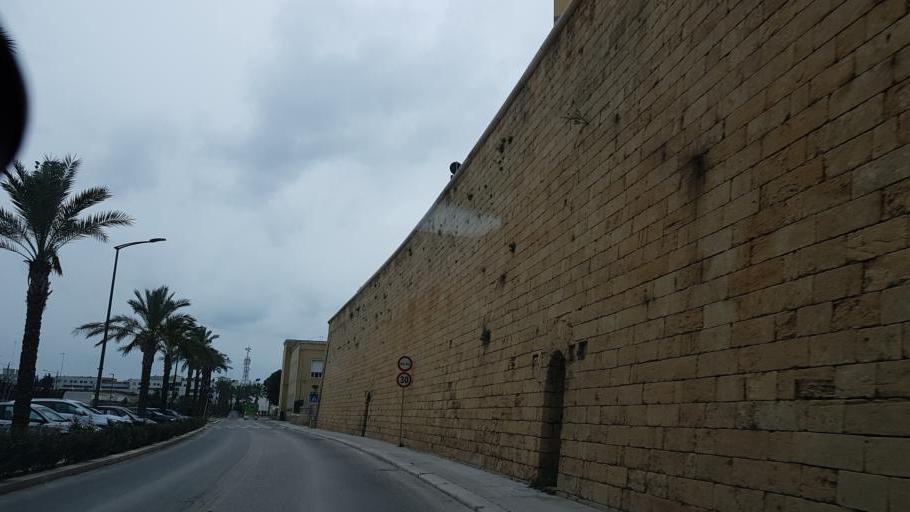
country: IT
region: Apulia
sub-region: Provincia di Brindisi
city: Brindisi
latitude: 40.6348
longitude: 17.9481
